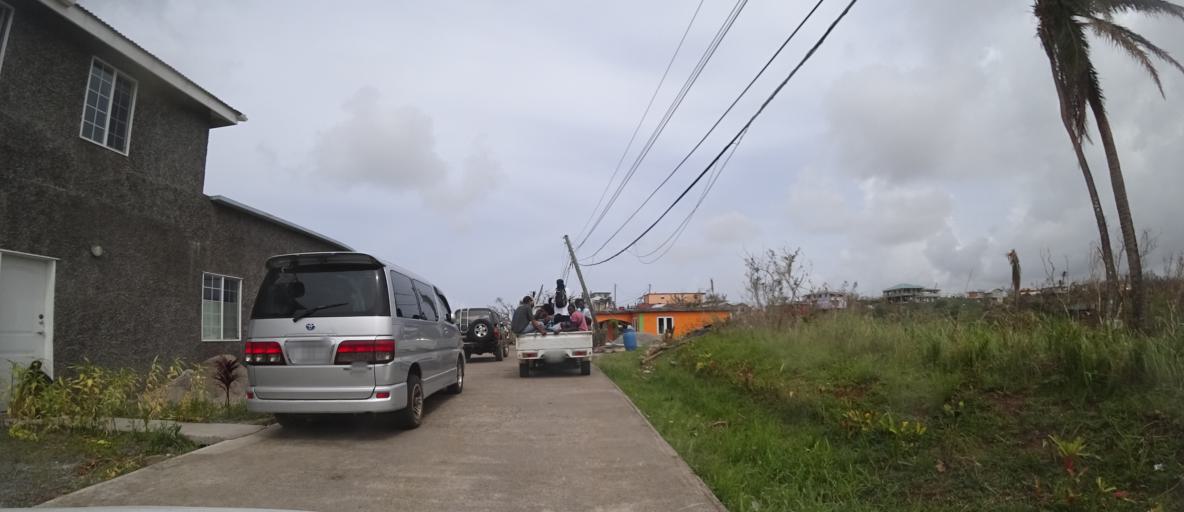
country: DM
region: Saint Andrew
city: Calibishie
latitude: 15.5853
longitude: -61.3736
